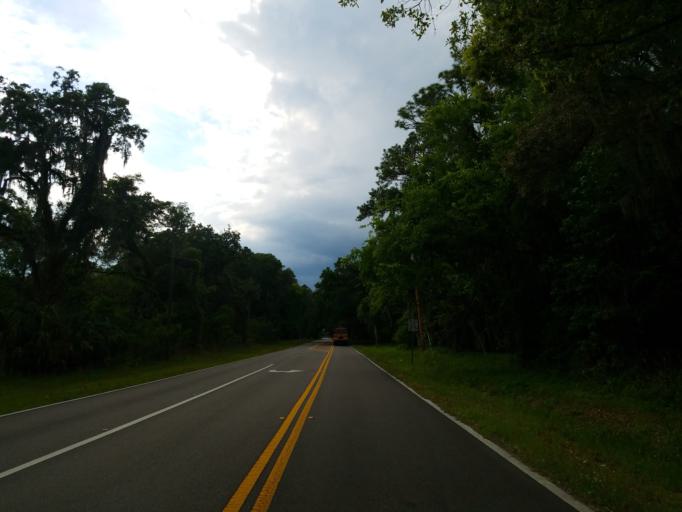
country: US
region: Florida
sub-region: Hernando County
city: Brooksville
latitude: 28.5557
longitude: -82.3636
